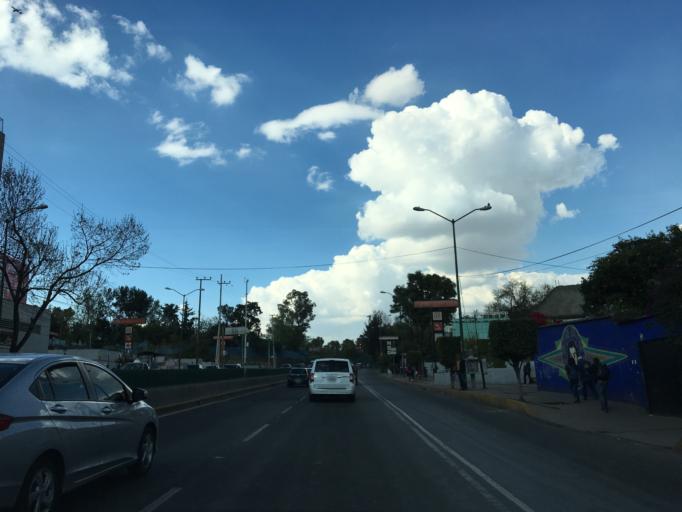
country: MX
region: Mexico City
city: Polanco
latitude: 19.4111
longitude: -99.1911
